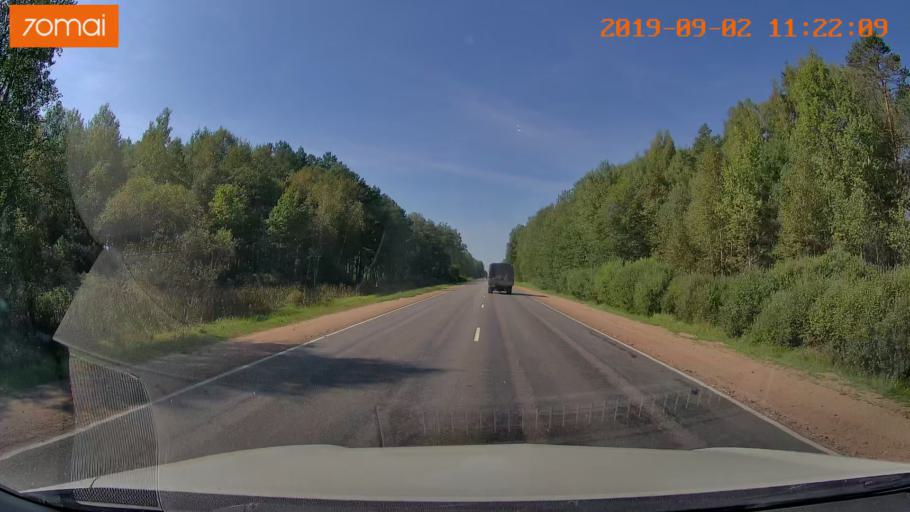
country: RU
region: Smolensk
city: Roslavl'
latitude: 54.0287
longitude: 33.0204
